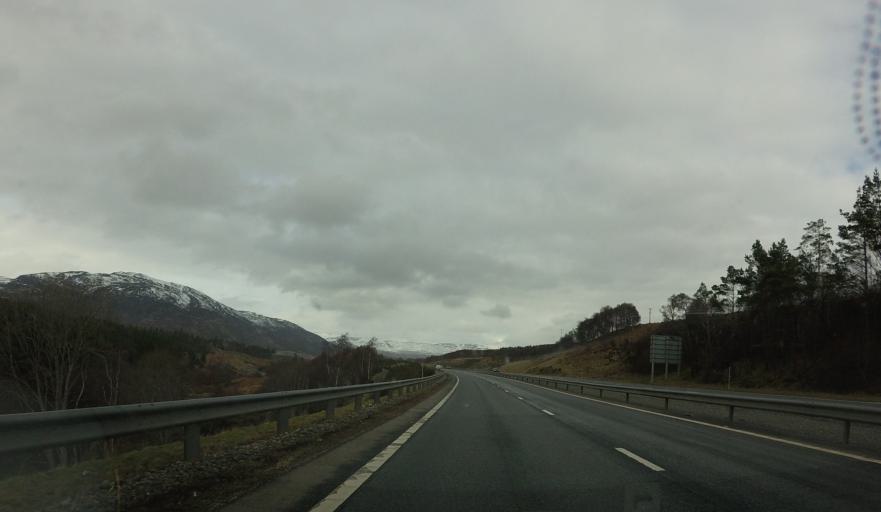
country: GB
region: Scotland
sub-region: Highland
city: Kingussie
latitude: 57.0151
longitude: -4.1619
